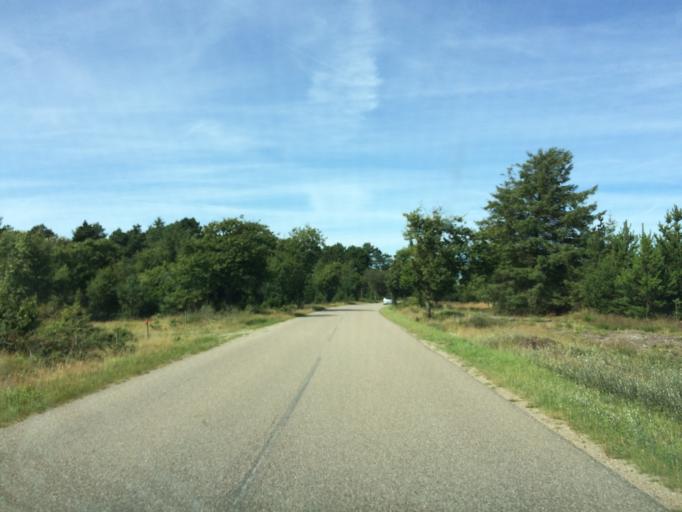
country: DK
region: South Denmark
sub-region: Varde Kommune
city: Oksbol
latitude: 55.6719
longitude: 8.1900
